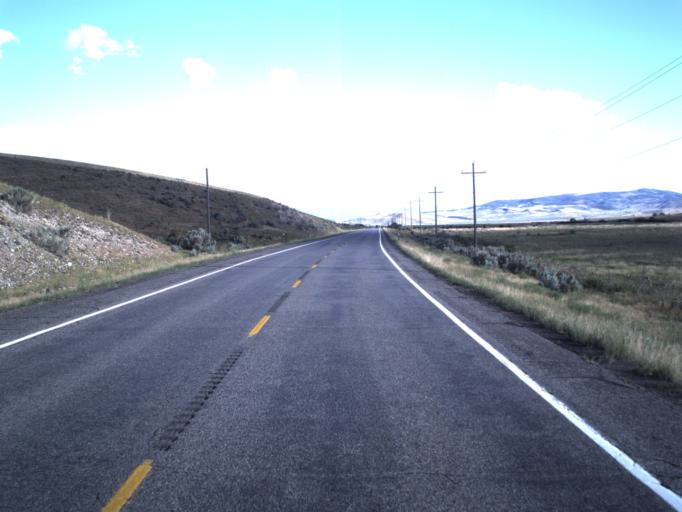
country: US
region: Utah
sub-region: Sanpete County
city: Fairview
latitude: 39.8213
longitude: -111.5085
